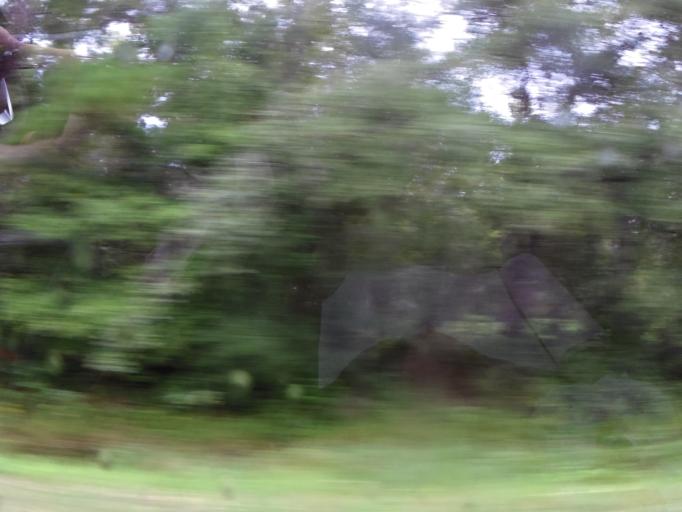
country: US
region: Florida
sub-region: Duval County
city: Baldwin
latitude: 30.4314
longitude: -82.0177
